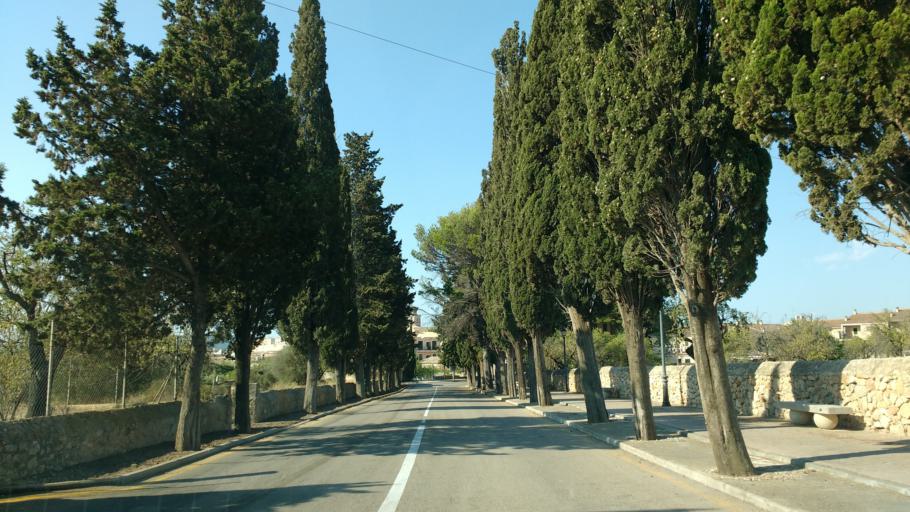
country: ES
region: Balearic Islands
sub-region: Illes Balears
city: Consell
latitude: 39.6718
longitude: 2.8147
